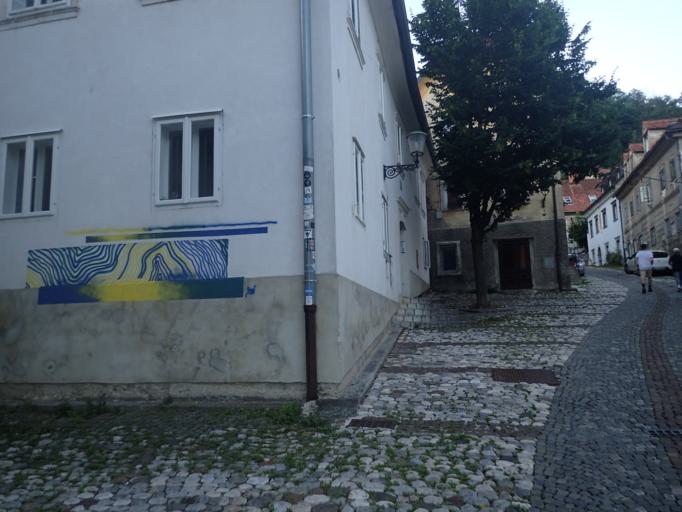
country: SI
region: Ljubljana
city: Ljubljana
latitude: 46.0453
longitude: 14.5072
